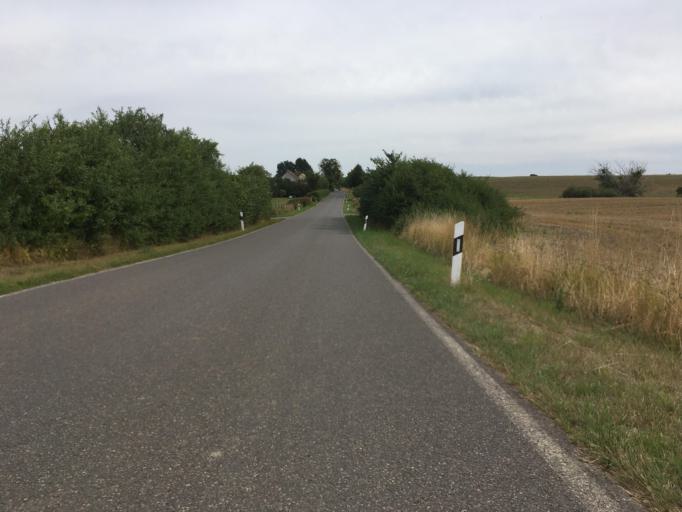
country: DE
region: Brandenburg
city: Gerswalde
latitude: 53.1368
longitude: 13.7420
